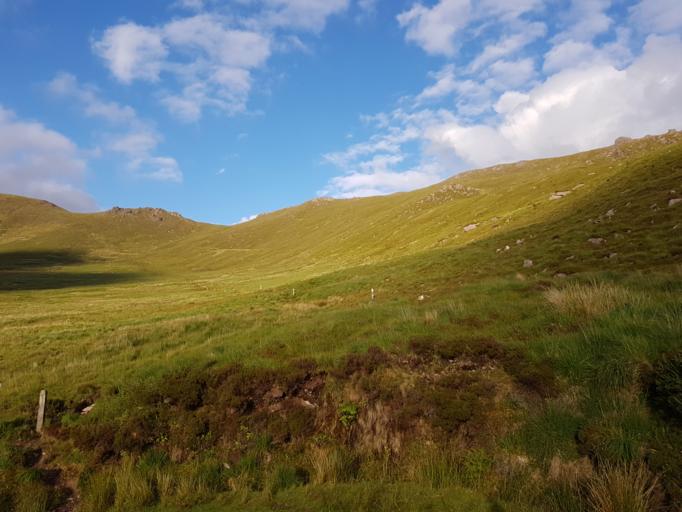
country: IE
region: Munster
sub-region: Ciarrai
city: Killorglin
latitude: 52.1880
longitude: -9.8775
